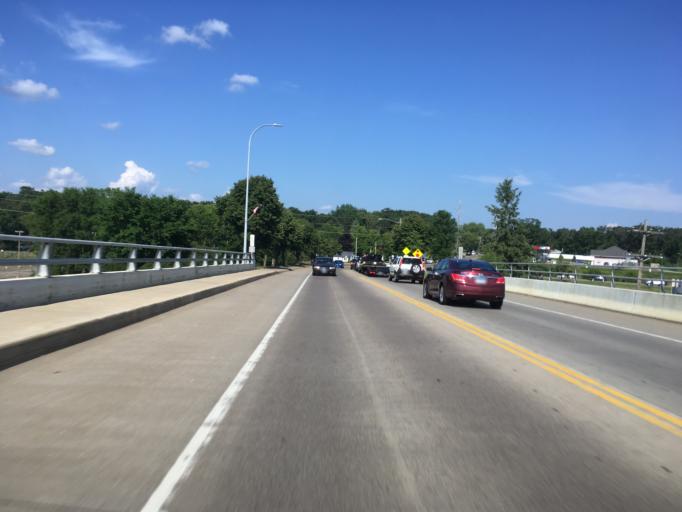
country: US
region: Minnesota
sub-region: Stearns County
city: Sartell
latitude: 45.6167
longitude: -94.1996
